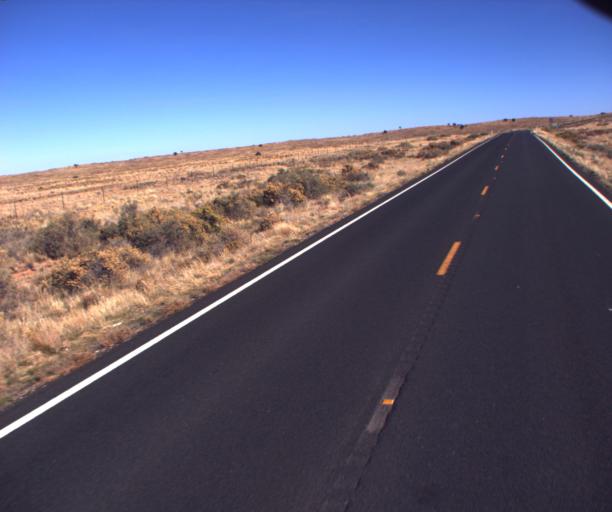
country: US
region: Arizona
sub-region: Apache County
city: Ganado
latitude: 35.7877
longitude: -109.6850
